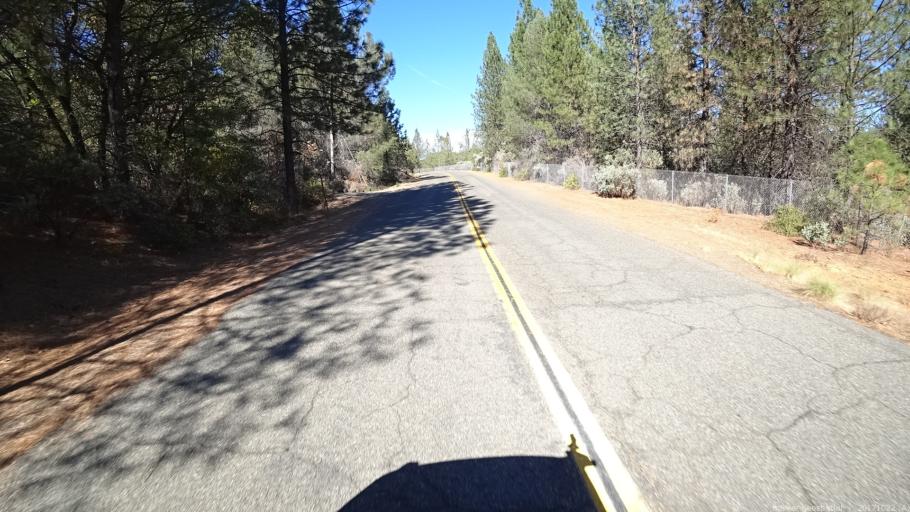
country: US
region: California
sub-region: Shasta County
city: Central Valley (historical)
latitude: 40.9103
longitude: -122.3871
